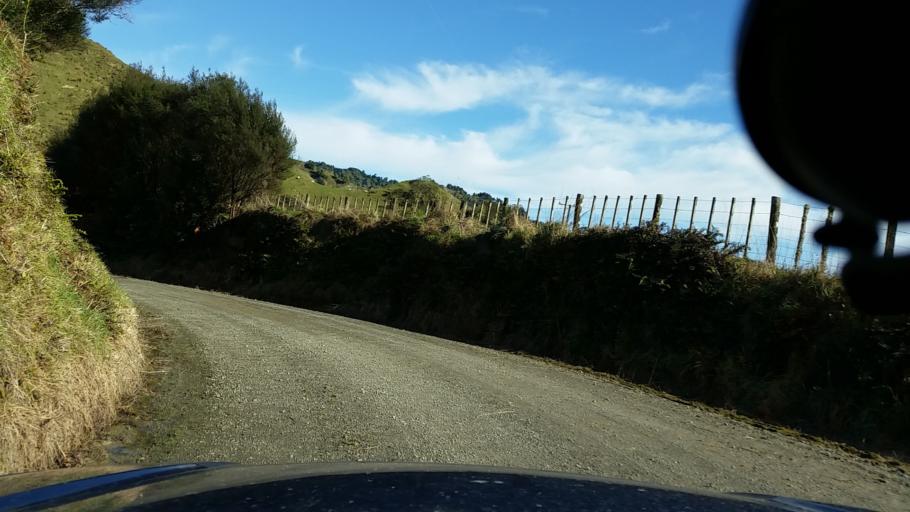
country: NZ
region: Taranaki
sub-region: New Plymouth District
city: Waitara
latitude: -39.0511
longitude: 174.7582
